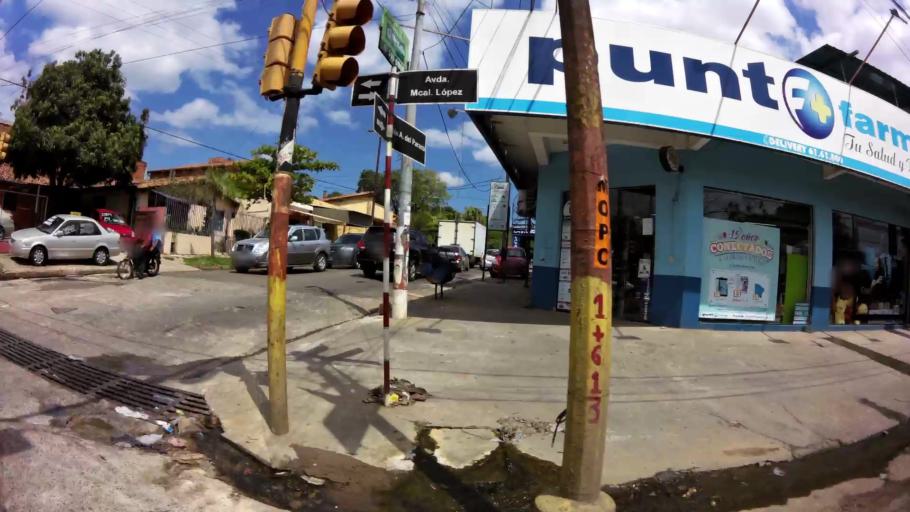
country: PY
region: Central
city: Fernando de la Mora
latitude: -25.3057
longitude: -57.5442
